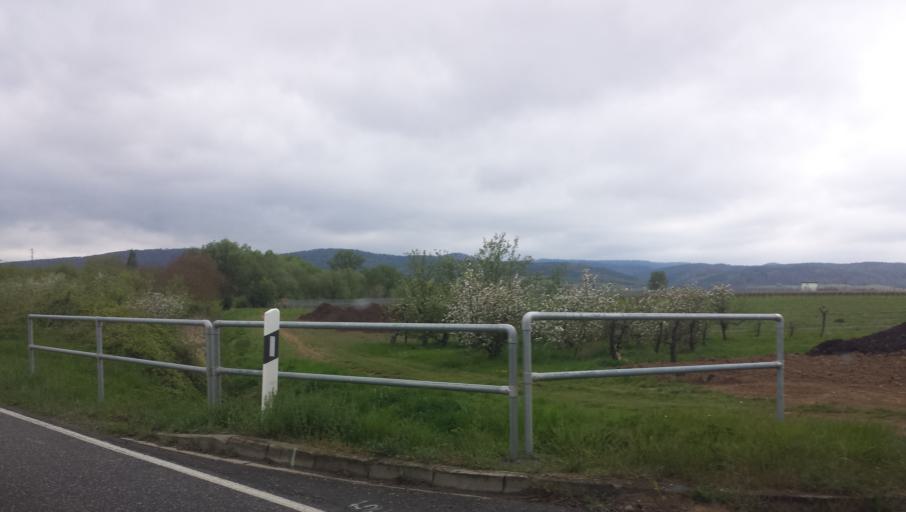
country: DE
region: Rheinland-Pfalz
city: Schweighofen
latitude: 49.0378
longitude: 7.9769
